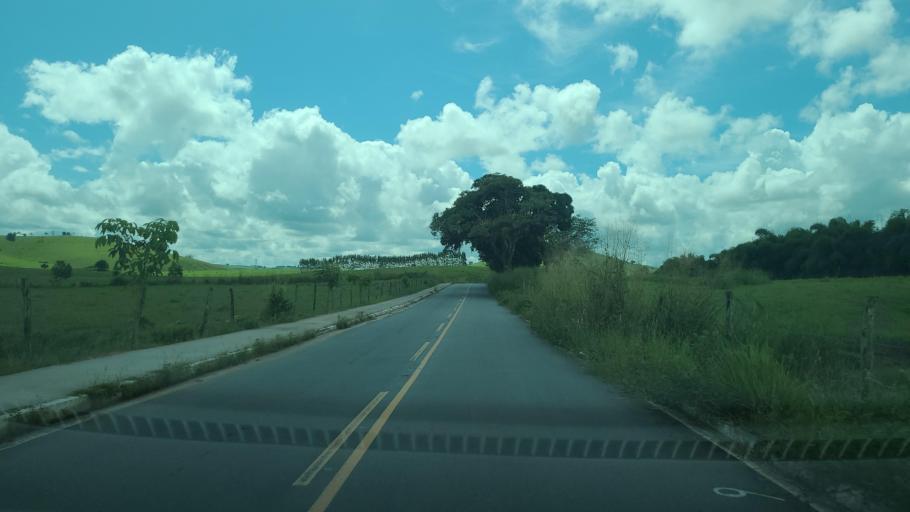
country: BR
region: Alagoas
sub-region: Uniao Dos Palmares
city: Uniao dos Palmares
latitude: -9.1593
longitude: -36.0451
